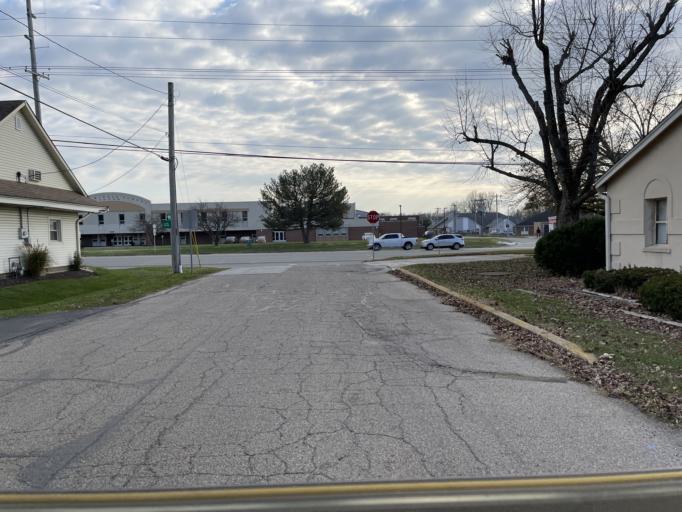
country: US
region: Indiana
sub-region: Hendricks County
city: Avon
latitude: 39.7633
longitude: -86.3966
